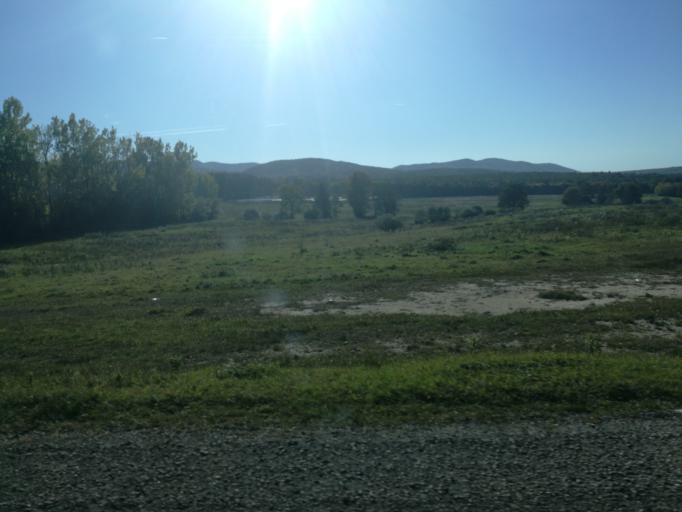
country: RO
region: Brasov
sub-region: Comuna Dumbravita
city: Dumbravita
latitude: 45.7471
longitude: 25.4131
